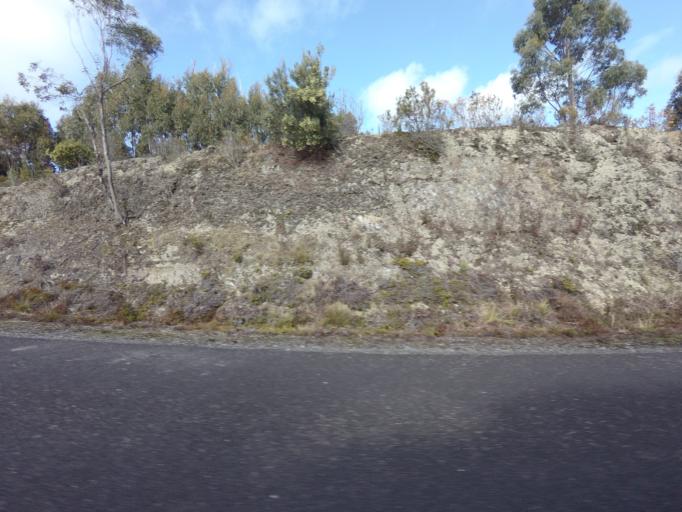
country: AU
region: Tasmania
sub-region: West Coast
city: Queenstown
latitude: -42.7989
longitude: 146.0905
